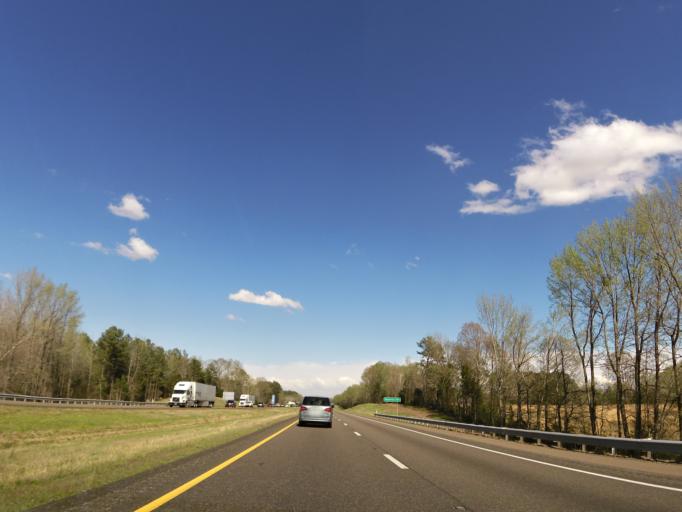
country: US
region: Tennessee
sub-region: Henderson County
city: Lexington
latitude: 35.7573
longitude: -88.5000
